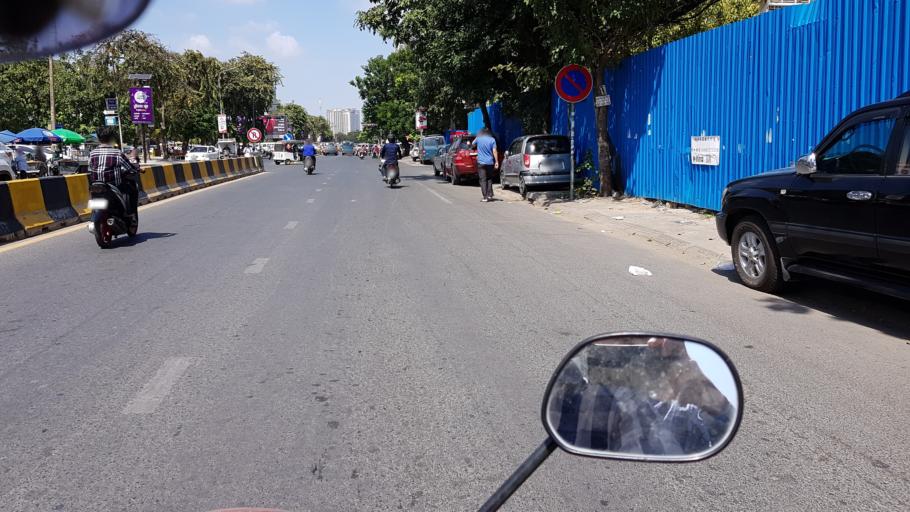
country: KH
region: Phnom Penh
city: Phnom Penh
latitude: 11.5668
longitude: 104.9116
